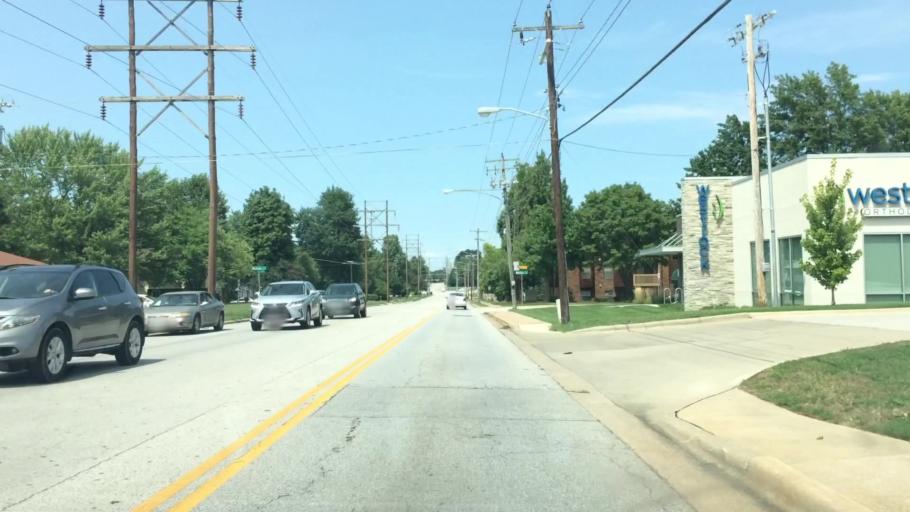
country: US
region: Missouri
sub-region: Greene County
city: Springfield
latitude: 37.1632
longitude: -93.2716
